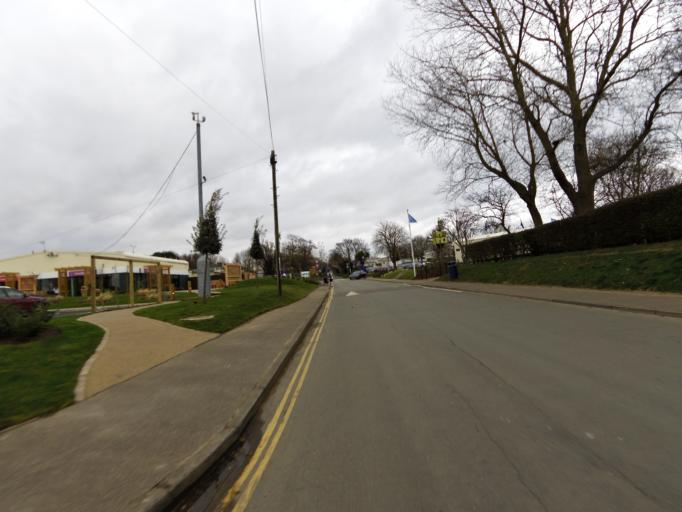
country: GB
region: England
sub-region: Norfolk
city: Hopton on Sea
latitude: 52.5409
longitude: 1.7324
